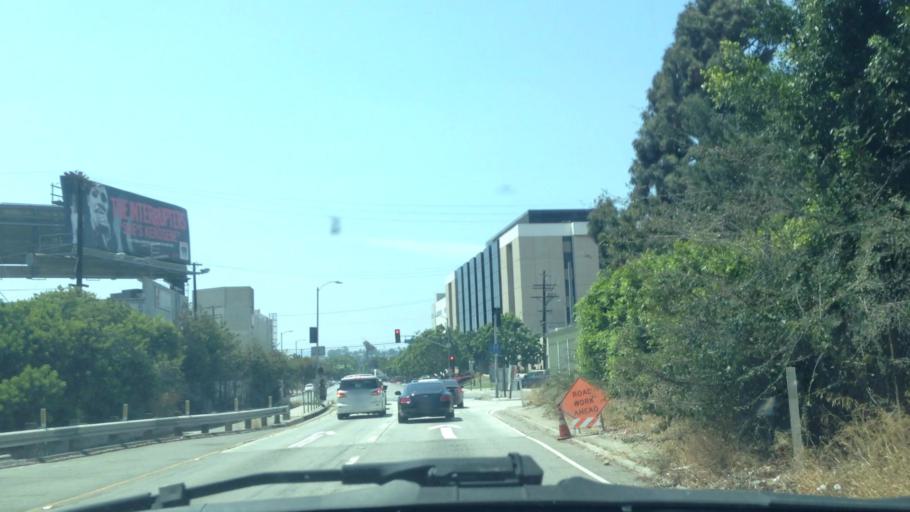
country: US
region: California
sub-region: Los Angeles County
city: Culver City
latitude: 34.0371
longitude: -118.3731
